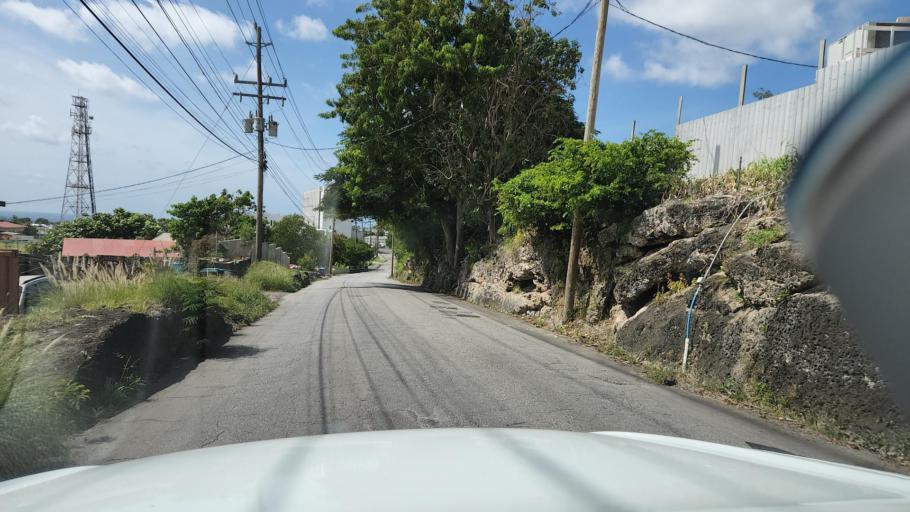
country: BB
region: Saint Michael
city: Bridgetown
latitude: 13.0930
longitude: -59.5764
